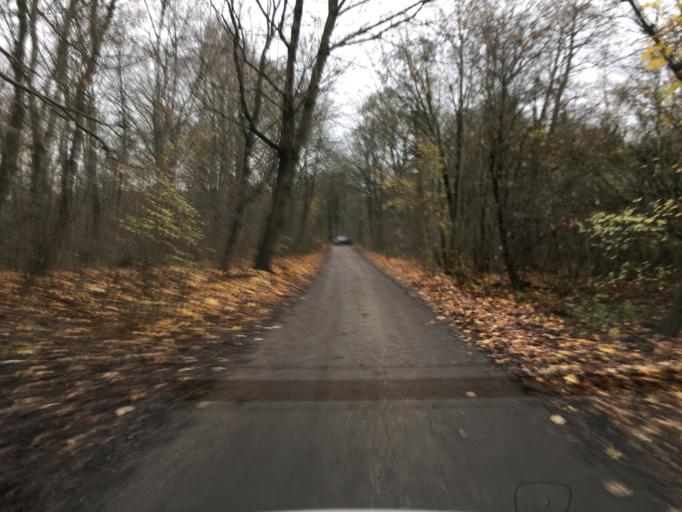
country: DK
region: South Denmark
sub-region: Tonder Kommune
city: Tonder
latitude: 54.9628
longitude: 8.8562
